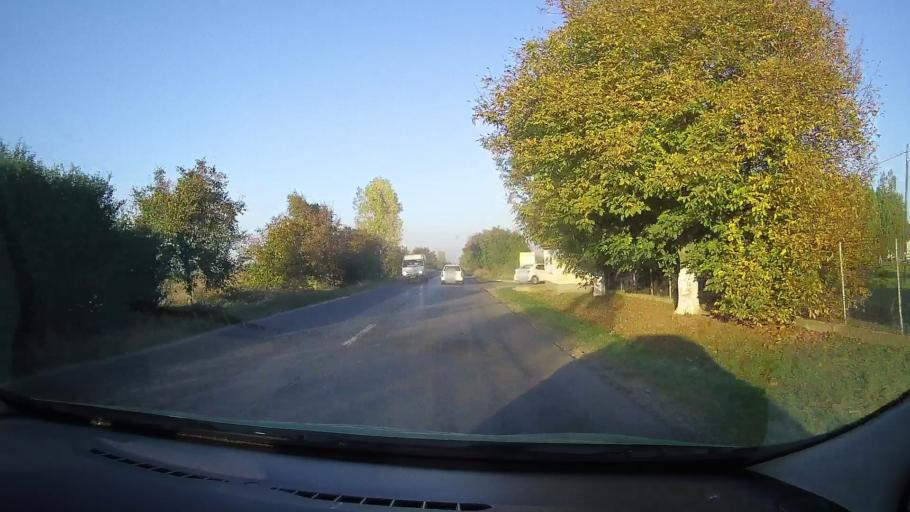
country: RO
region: Bihor
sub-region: Comuna Biharea
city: Biharea
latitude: 47.1735
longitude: 21.9615
